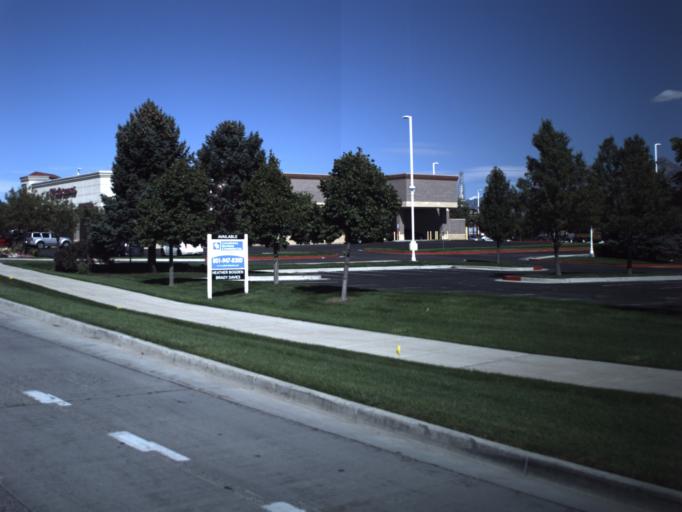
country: US
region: Utah
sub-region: Salt Lake County
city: South Jordan
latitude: 40.5608
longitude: -111.9386
